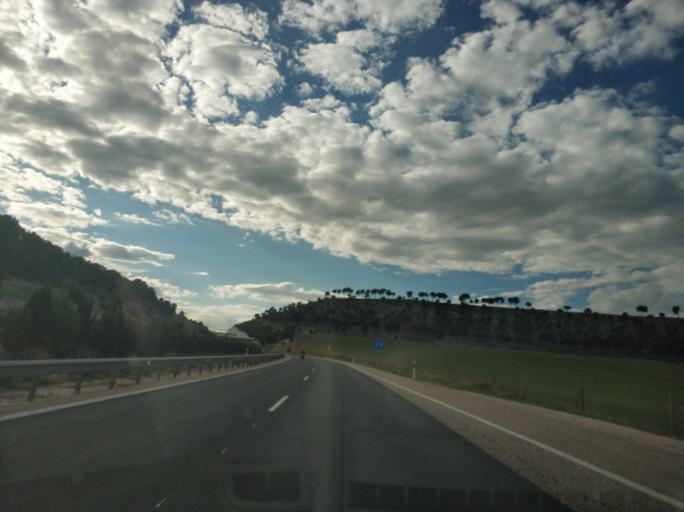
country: ES
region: Castille and Leon
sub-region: Provincia de Valladolid
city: Cisterniga
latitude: 41.6062
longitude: -4.6645
